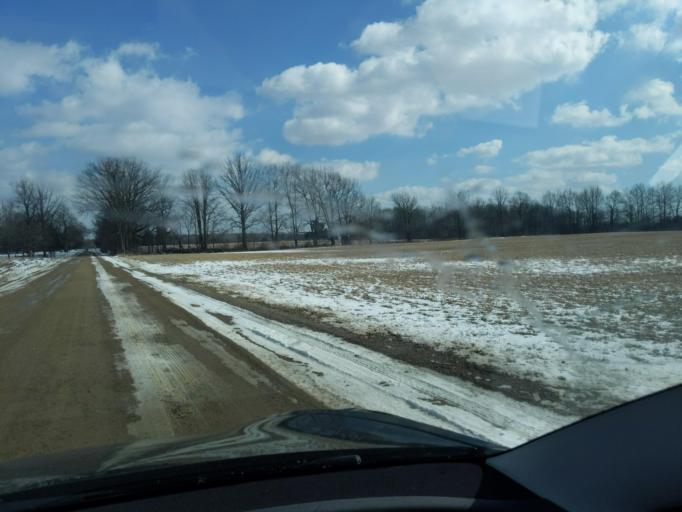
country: US
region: Michigan
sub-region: Livingston County
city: Fowlerville
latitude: 42.6139
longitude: -84.0973
